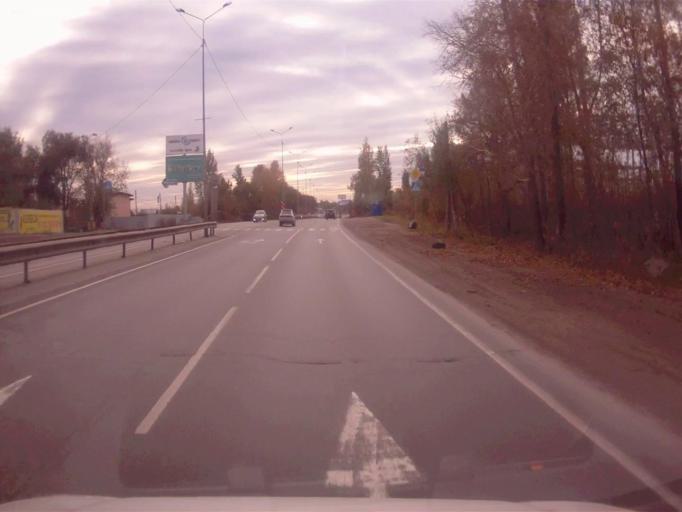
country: RU
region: Chelyabinsk
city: Novosineglazovskiy
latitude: 55.0860
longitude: 61.3973
